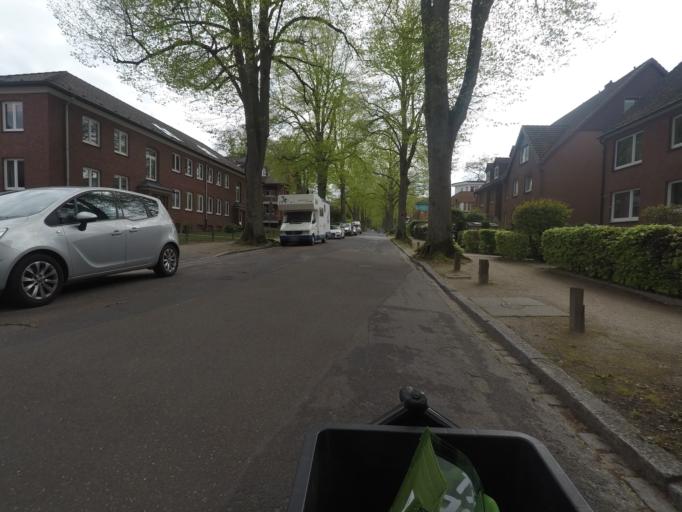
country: DE
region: Hamburg
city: Bergstedt
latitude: 53.6461
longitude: 10.1680
